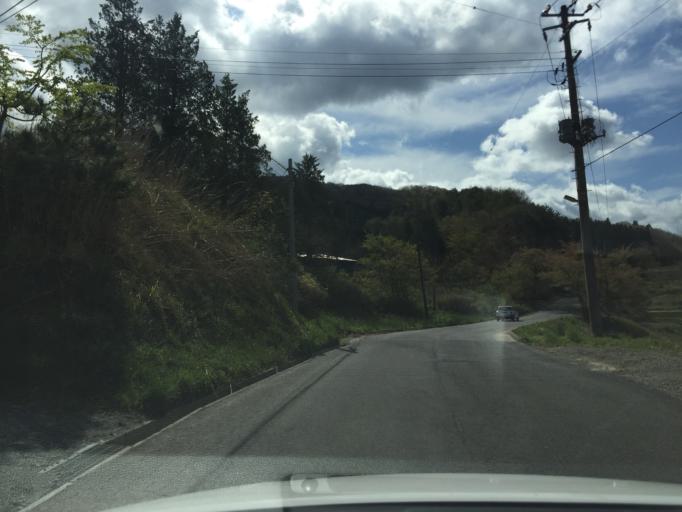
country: JP
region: Fukushima
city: Funehikimachi-funehiki
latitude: 37.5768
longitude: 140.6917
